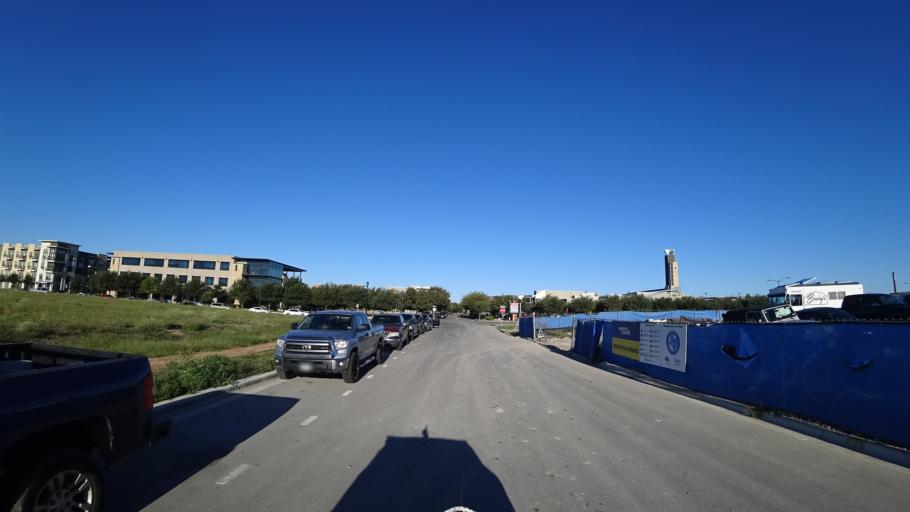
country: US
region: Texas
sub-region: Travis County
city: Austin
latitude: 30.3008
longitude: -97.7051
